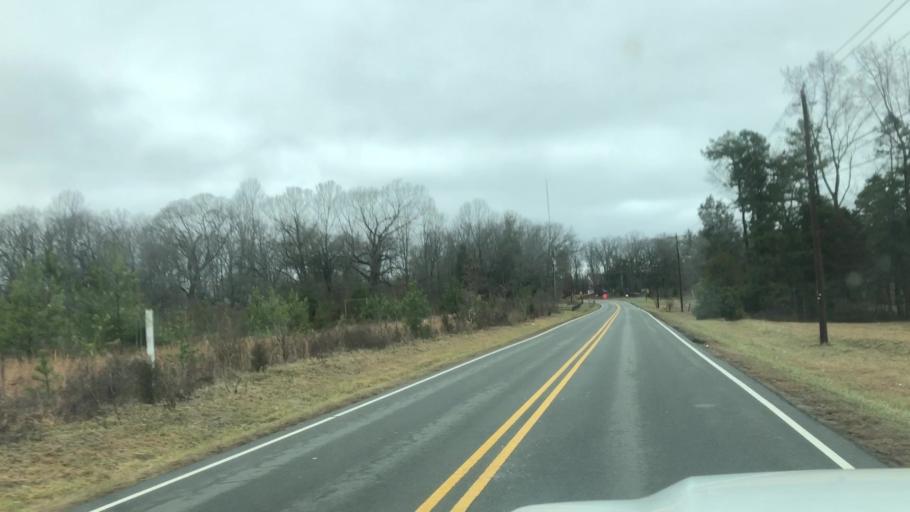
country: US
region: North Carolina
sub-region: Mecklenburg County
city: Mint Hill
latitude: 35.2384
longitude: -80.6715
